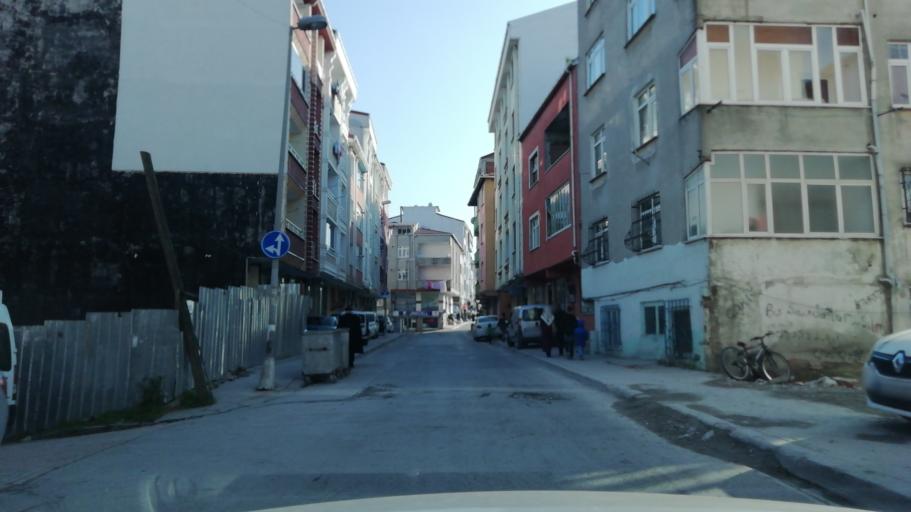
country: TR
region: Istanbul
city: Esenyurt
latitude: 41.0314
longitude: 28.6893
